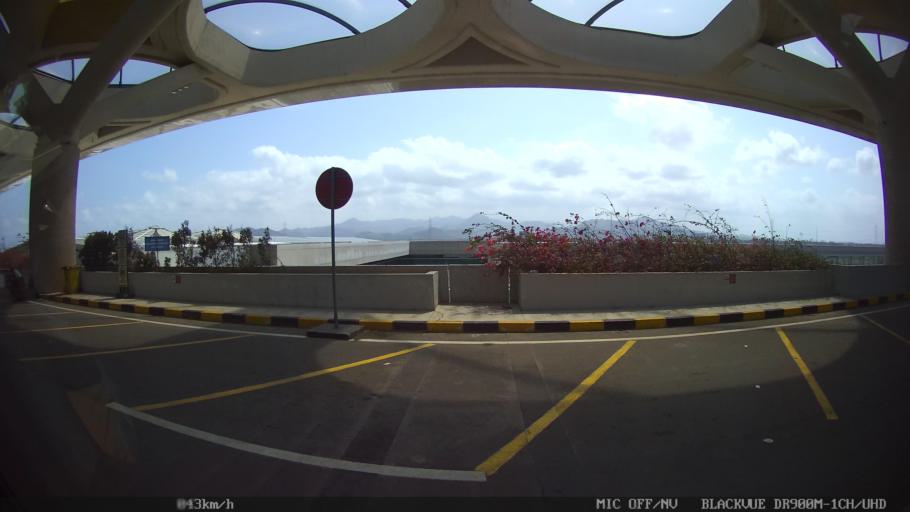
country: ID
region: Daerah Istimewa Yogyakarta
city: Srandakan
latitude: -7.8975
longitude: 110.0598
